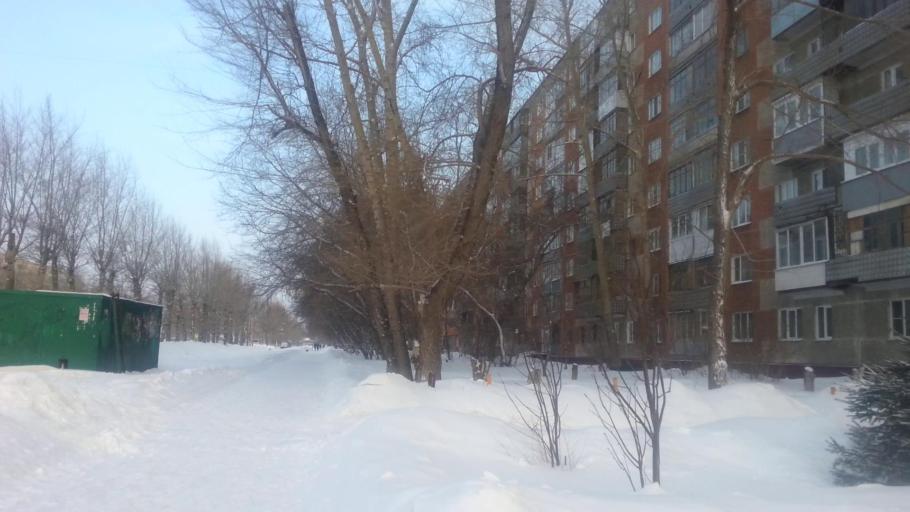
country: RU
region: Altai Krai
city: Novosilikatnyy
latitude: 53.3625
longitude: 83.6761
